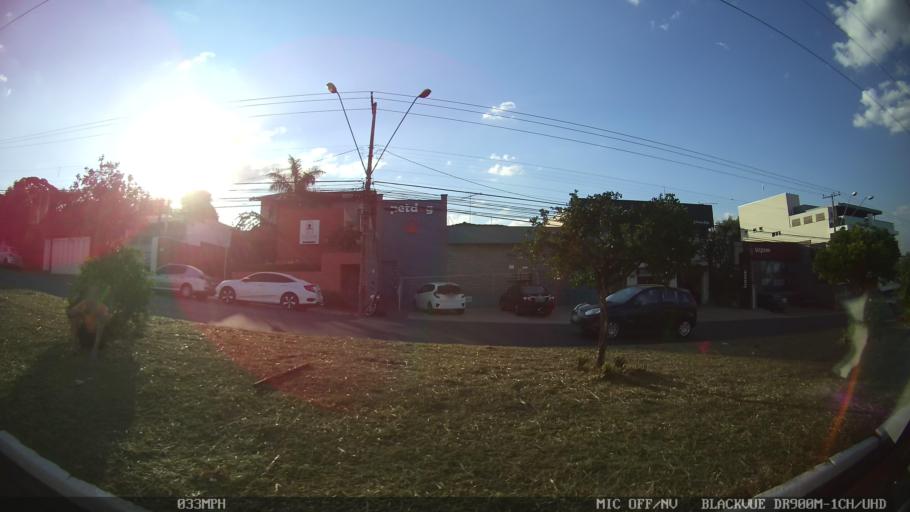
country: BR
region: Sao Paulo
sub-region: Ribeirao Preto
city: Ribeirao Preto
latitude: -21.1950
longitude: -47.8043
